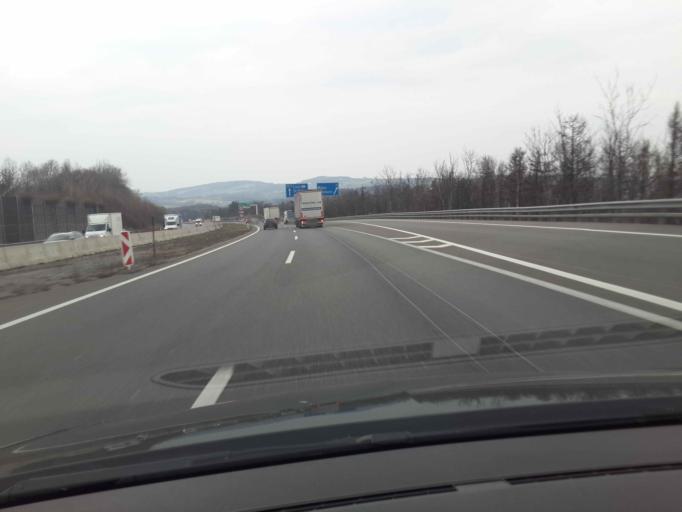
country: AT
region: Lower Austria
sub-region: Politischer Bezirk Sankt Polten
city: Eichgraben
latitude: 48.1487
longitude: 15.9808
